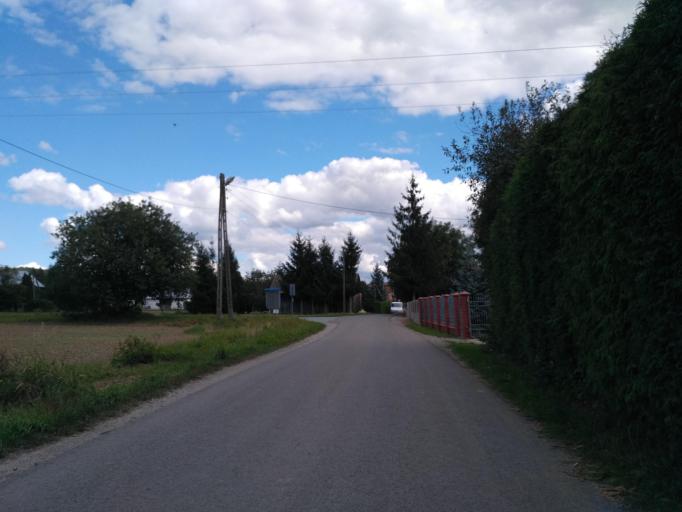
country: PL
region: Subcarpathian Voivodeship
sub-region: Powiat jasielski
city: Jaslo
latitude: 49.7638
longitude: 21.5259
